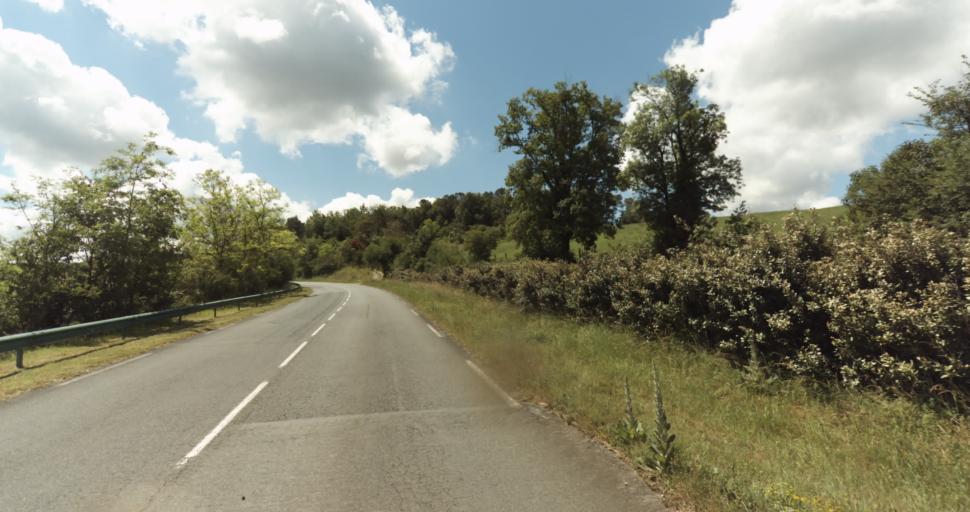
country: FR
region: Aquitaine
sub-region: Departement de la Dordogne
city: Beaumont-du-Perigord
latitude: 44.7827
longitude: 0.7660
